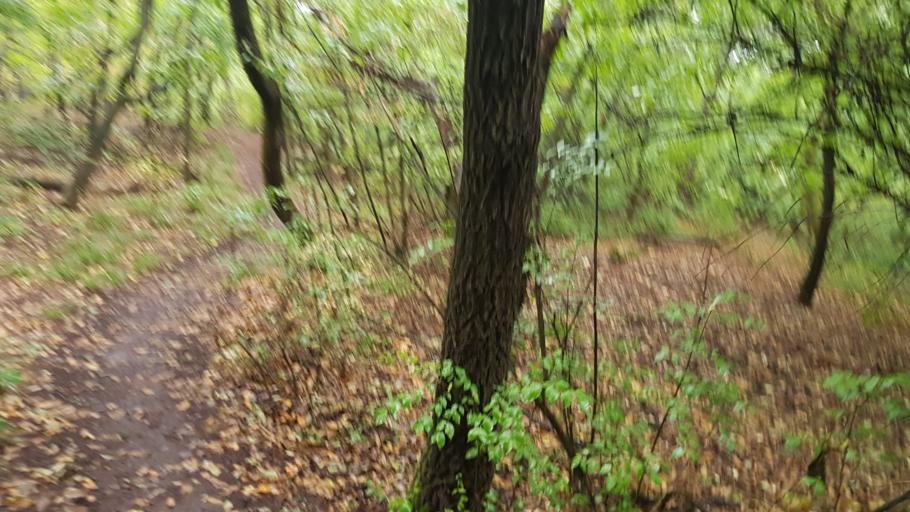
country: HU
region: Pest
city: Toeroekbalint
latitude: 47.4663
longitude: 18.9200
